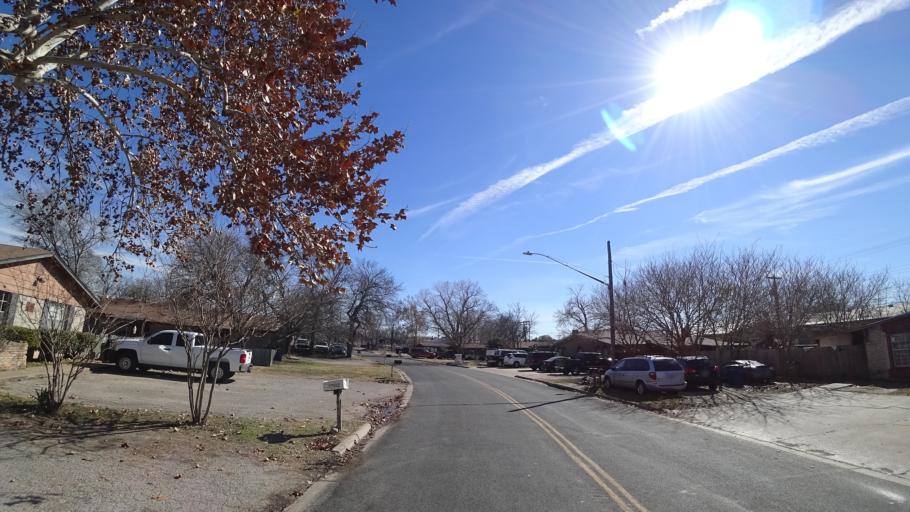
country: US
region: Texas
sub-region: Travis County
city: Wells Branch
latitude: 30.3749
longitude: -97.6923
